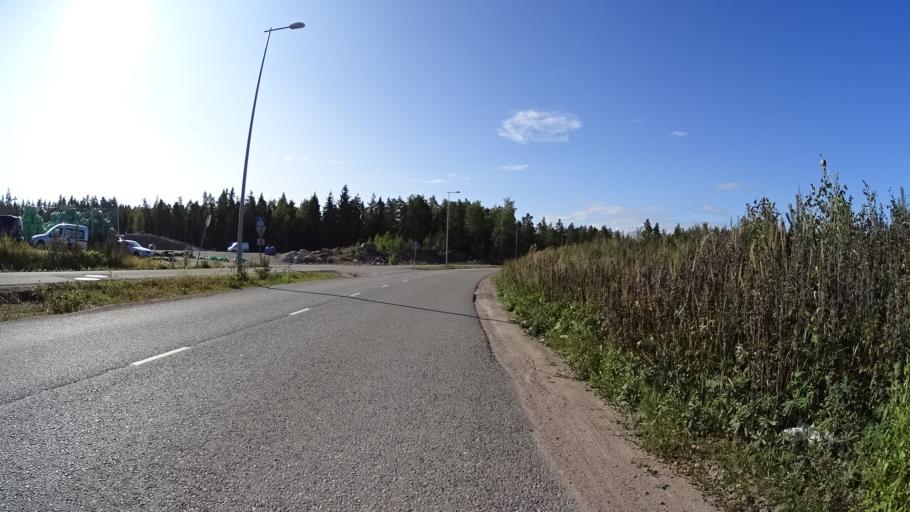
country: FI
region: Uusimaa
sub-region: Helsinki
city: Kilo
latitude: 60.2895
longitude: 24.7659
